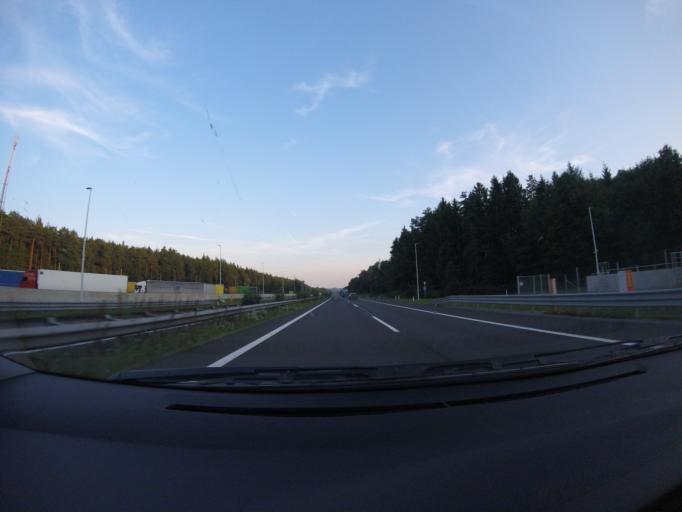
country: AT
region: Styria
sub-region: Politischer Bezirk Hartberg-Fuerstenfeld
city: Hainersdorf
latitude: 47.1174
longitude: 15.9843
